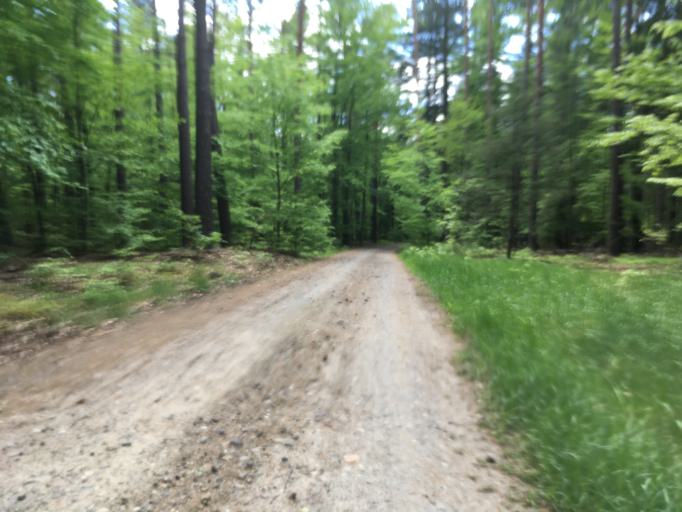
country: DE
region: Brandenburg
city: Marienwerder
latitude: 52.8233
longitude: 13.6270
